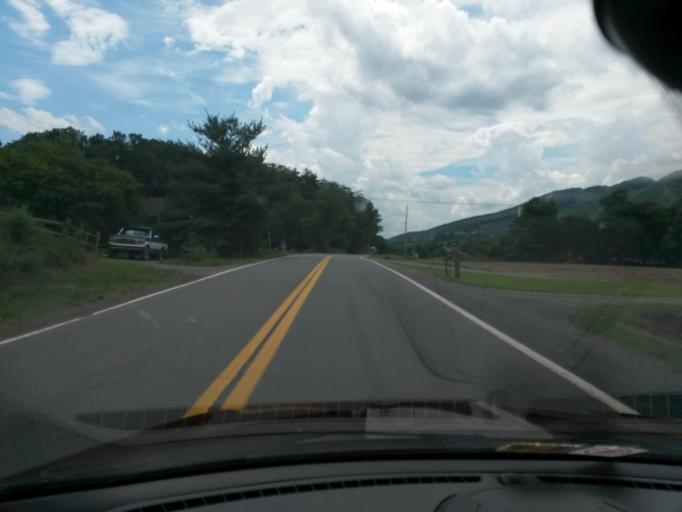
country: US
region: West Virginia
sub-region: Grant County
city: Petersburg
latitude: 38.9063
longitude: -79.1911
